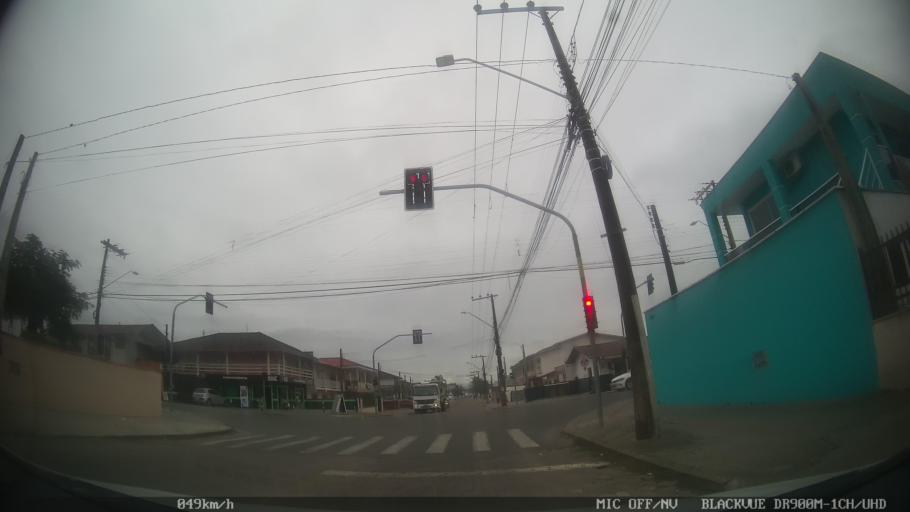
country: BR
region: Santa Catarina
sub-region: Joinville
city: Joinville
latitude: -26.3339
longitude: -48.8136
